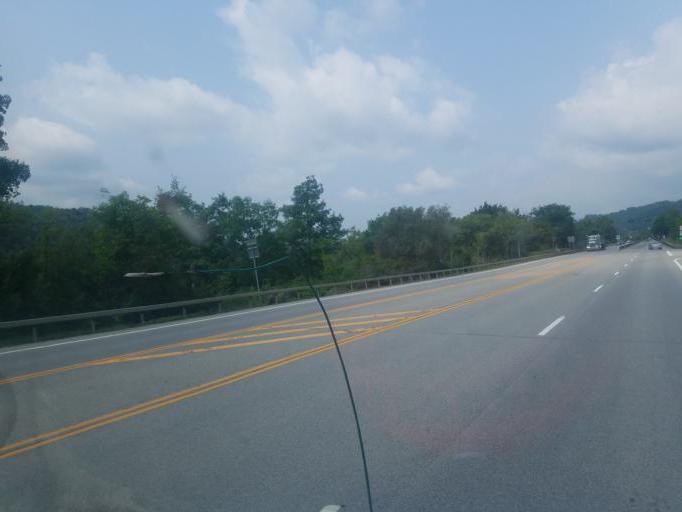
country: US
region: New York
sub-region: Herkimer County
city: Little Falls
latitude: 43.0383
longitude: -74.8387
